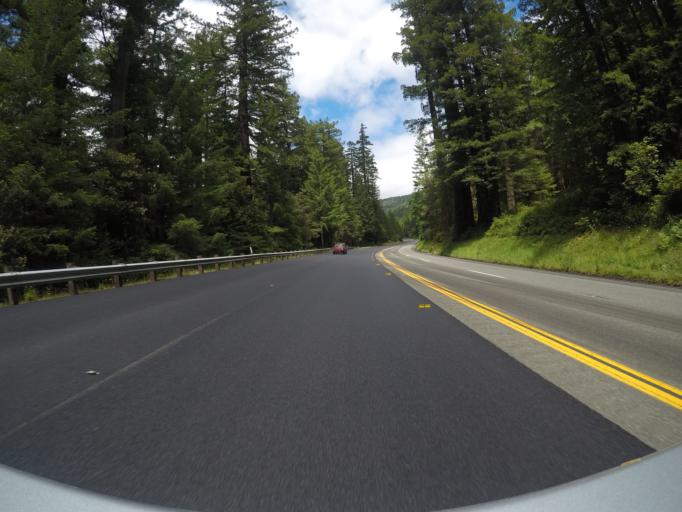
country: US
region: California
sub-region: Humboldt County
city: Redway
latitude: 40.2904
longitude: -123.8962
